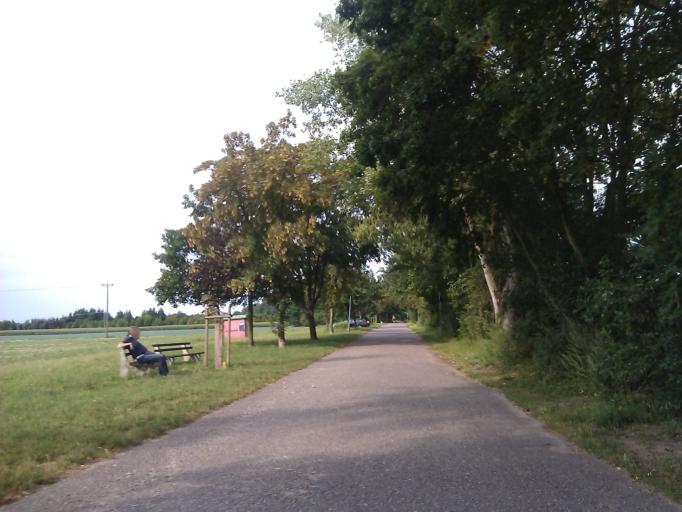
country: DE
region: Rheinland-Pfalz
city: Neuhofen
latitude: 49.4154
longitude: 8.4186
